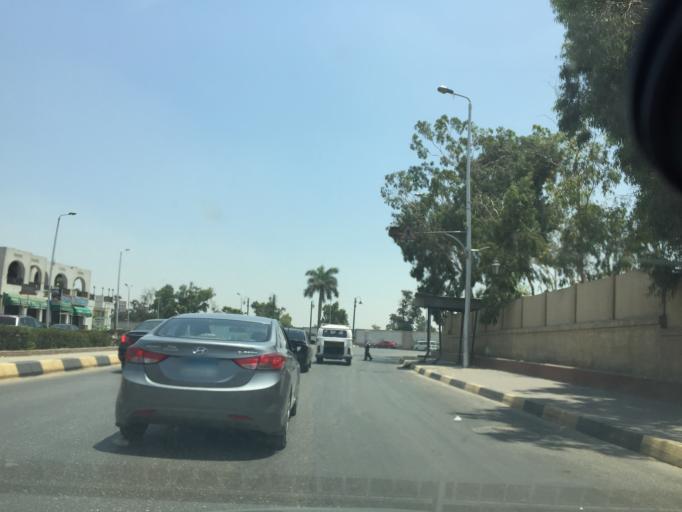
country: EG
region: Al Jizah
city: Al Jizah
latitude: 29.9854
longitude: 31.1350
